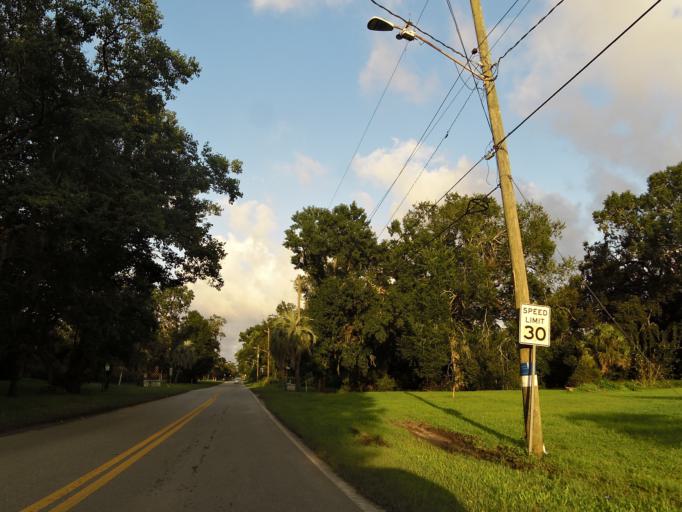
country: US
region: Florida
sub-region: Duval County
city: Jacksonville
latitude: 30.3259
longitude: -81.7006
